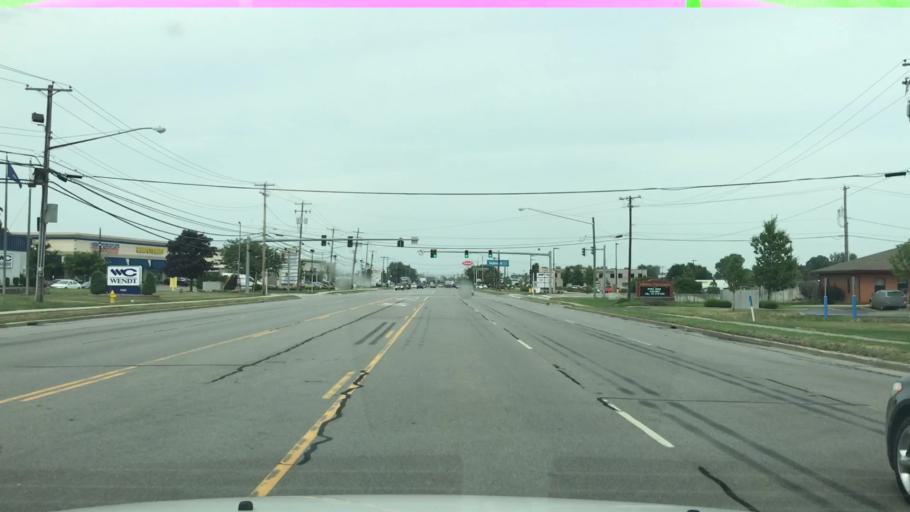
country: US
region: New York
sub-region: Erie County
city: Cheektowaga
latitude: 42.9086
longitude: -78.7408
